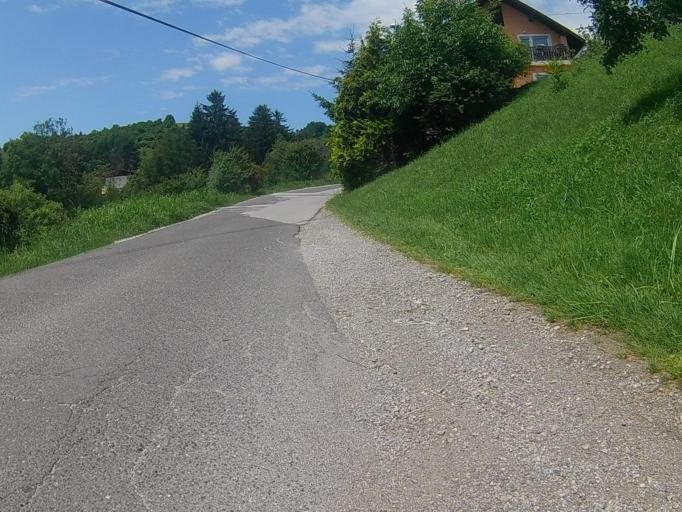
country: SI
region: Maribor
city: Kamnica
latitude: 46.5747
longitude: 15.6218
